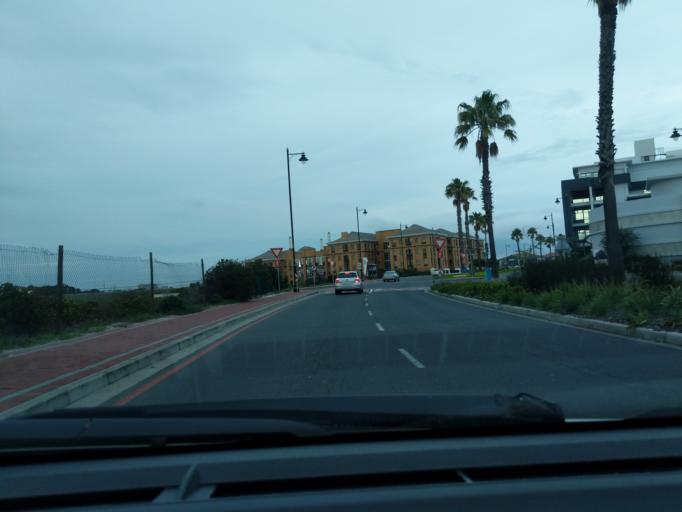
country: ZA
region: Western Cape
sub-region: City of Cape Town
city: Sunset Beach
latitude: -33.8861
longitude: 18.5202
